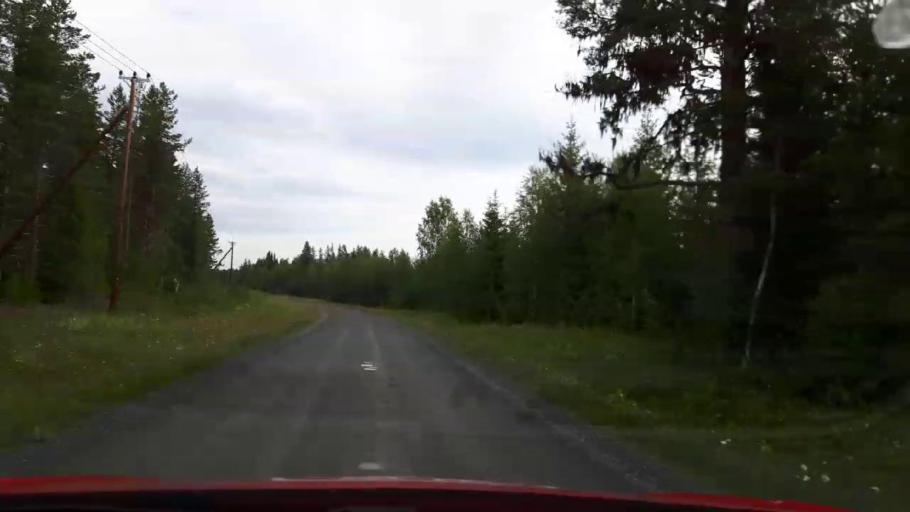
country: SE
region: Jaemtland
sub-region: Stroemsunds Kommun
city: Stroemsund
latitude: 63.4995
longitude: 15.3287
